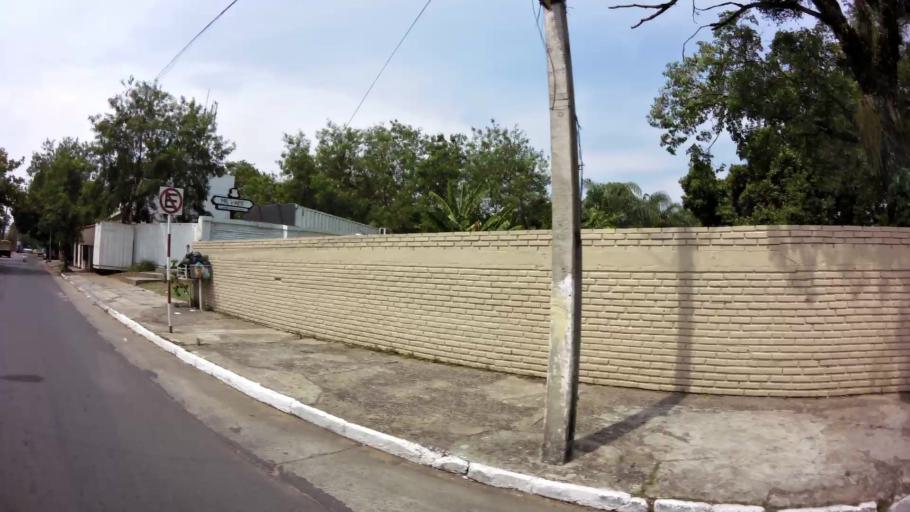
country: PY
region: Asuncion
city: Asuncion
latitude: -25.2849
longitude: -57.5908
